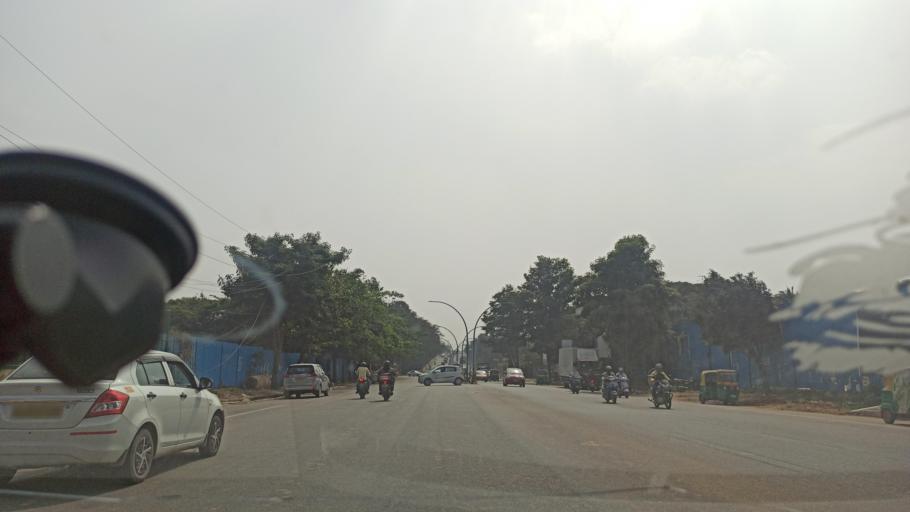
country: IN
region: Karnataka
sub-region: Bangalore Urban
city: Yelahanka
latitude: 13.0902
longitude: 77.5941
